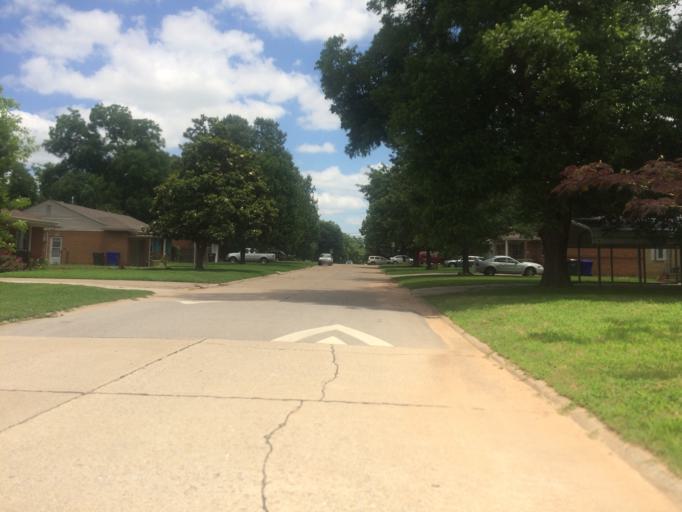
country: US
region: Oklahoma
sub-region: Cleveland County
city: Norman
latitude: 35.2075
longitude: -97.4603
